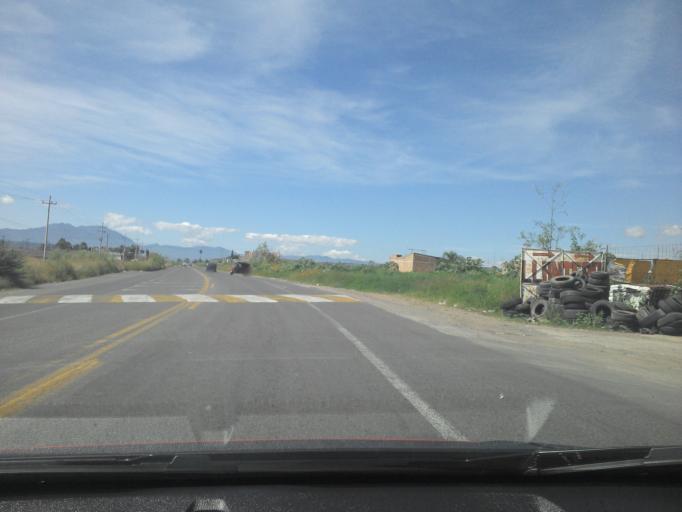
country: MX
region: Jalisco
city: El Refugio
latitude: 20.6668
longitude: -103.7396
